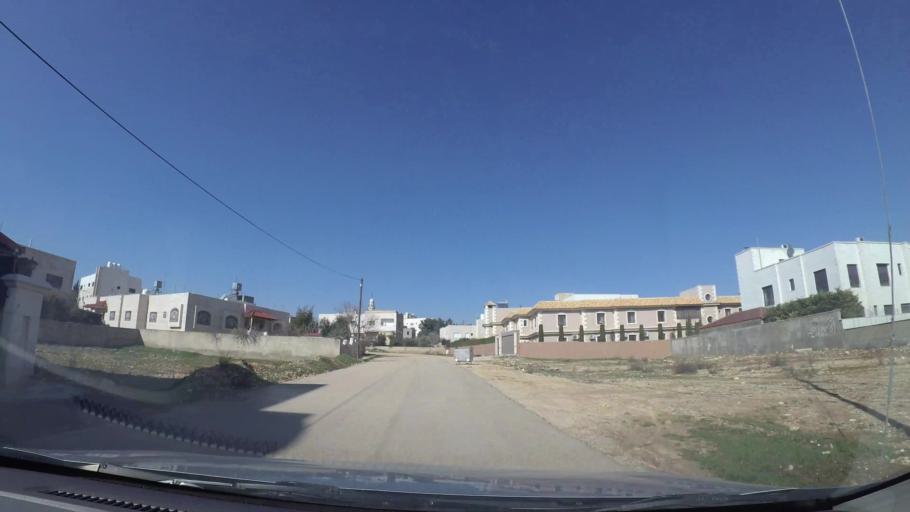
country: JO
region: Amman
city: Al Bunayyat ash Shamaliyah
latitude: 31.9058
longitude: 35.8911
